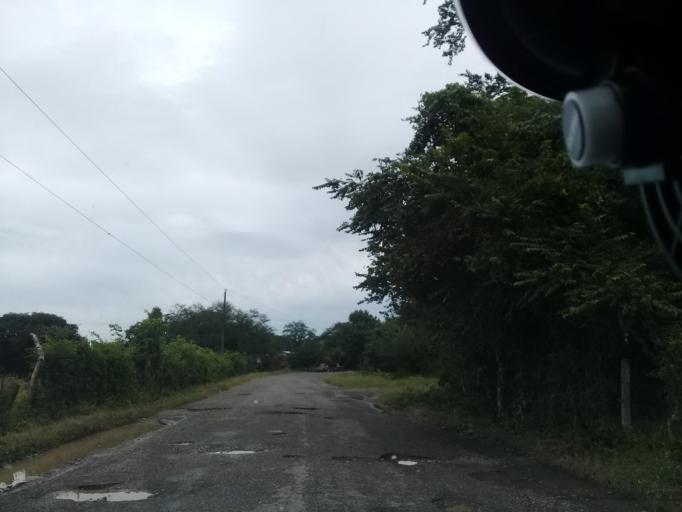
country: MX
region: Hidalgo
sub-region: Huejutla de Reyes
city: Chalahuiyapa
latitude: 21.1896
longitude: -98.3057
